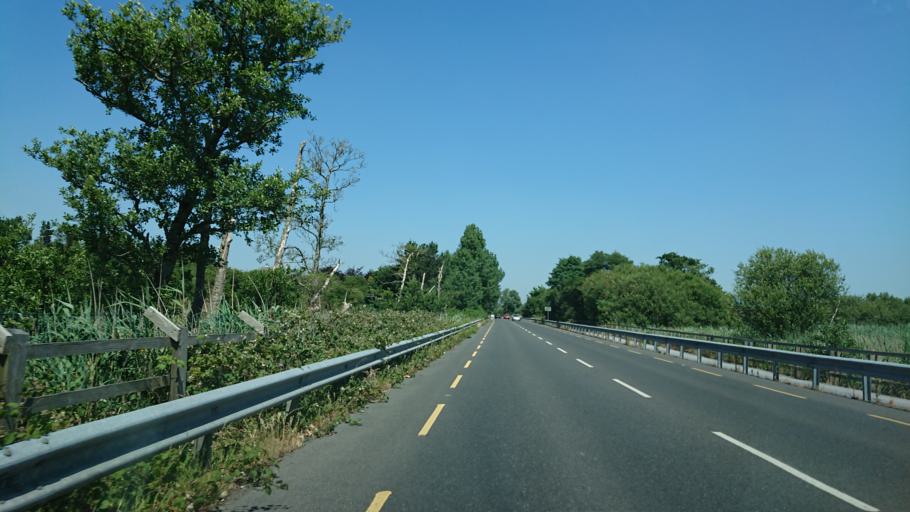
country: IE
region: Munster
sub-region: Waterford
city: Waterford
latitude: 52.2266
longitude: -7.1251
